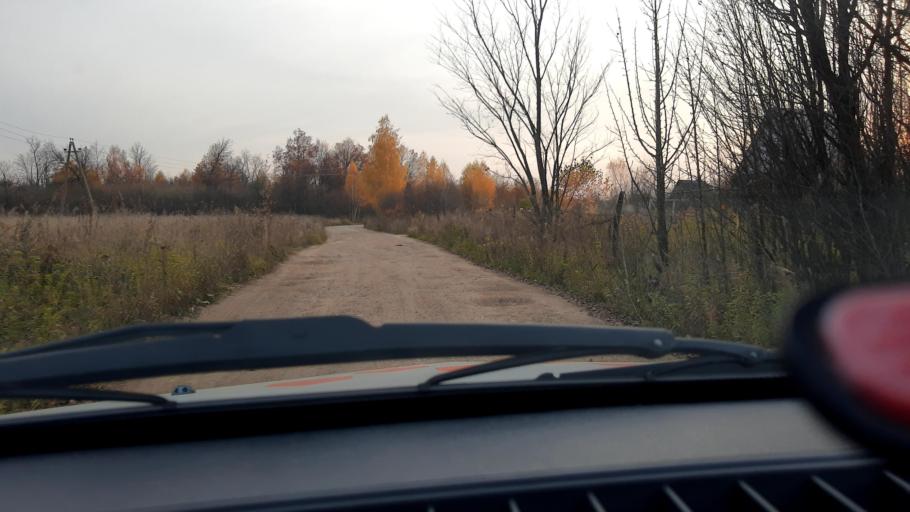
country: RU
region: Bashkortostan
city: Iglino
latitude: 54.7977
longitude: 56.3393
